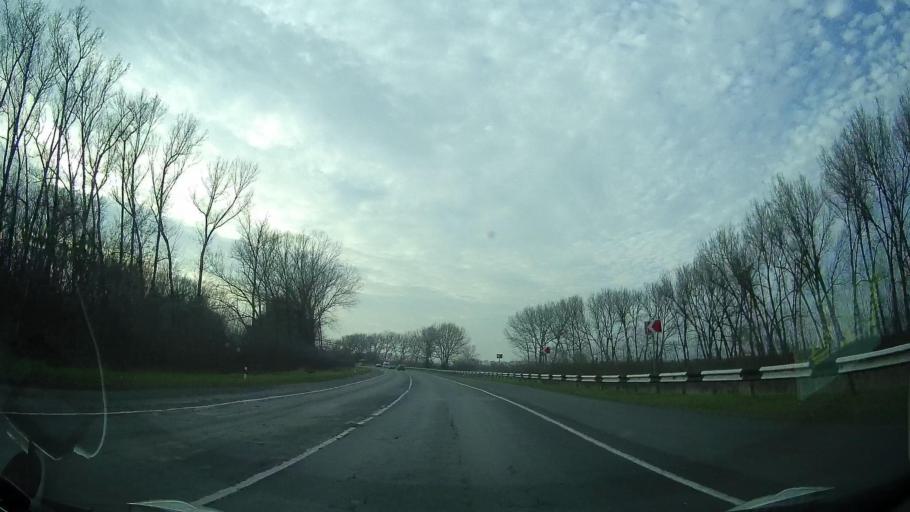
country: RU
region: Rostov
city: Starocherkasskaya
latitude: 47.1555
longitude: 40.1897
